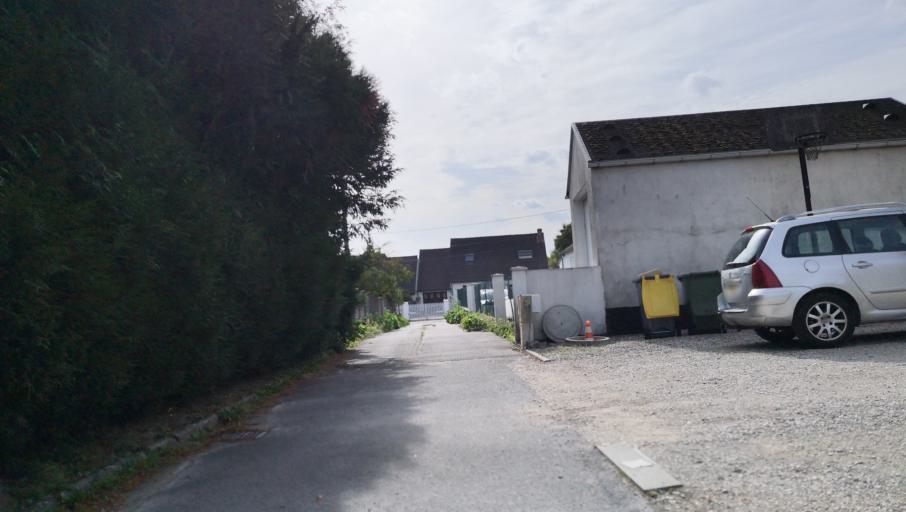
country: FR
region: Centre
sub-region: Departement du Loiret
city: Saint-Jean-de-la-Ruelle
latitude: 47.9234
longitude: 1.8672
